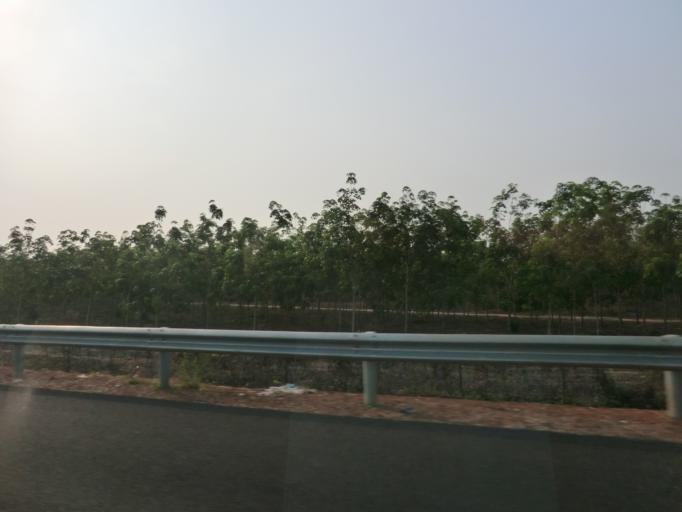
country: VN
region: Dong Nai
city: Long Thanh
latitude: 10.7748
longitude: 107.0059
